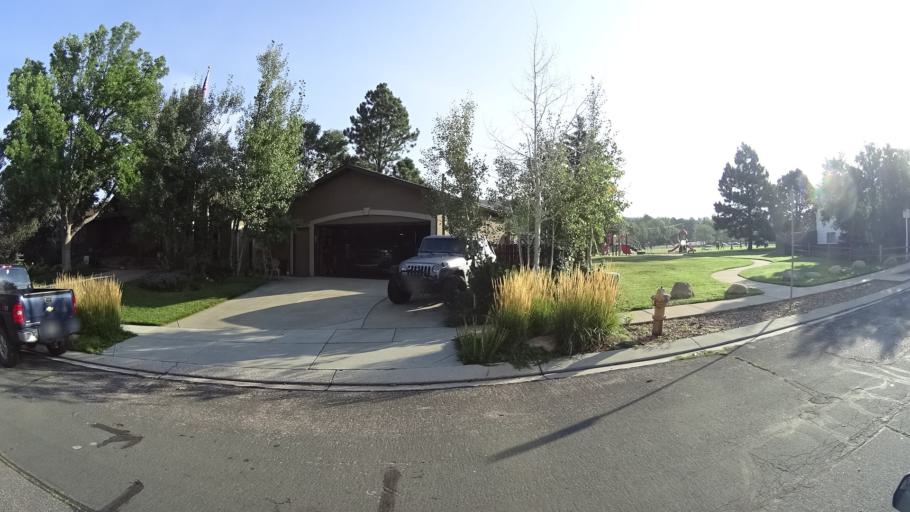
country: US
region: Colorado
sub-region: El Paso County
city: Colorado Springs
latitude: 38.8886
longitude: -104.8064
